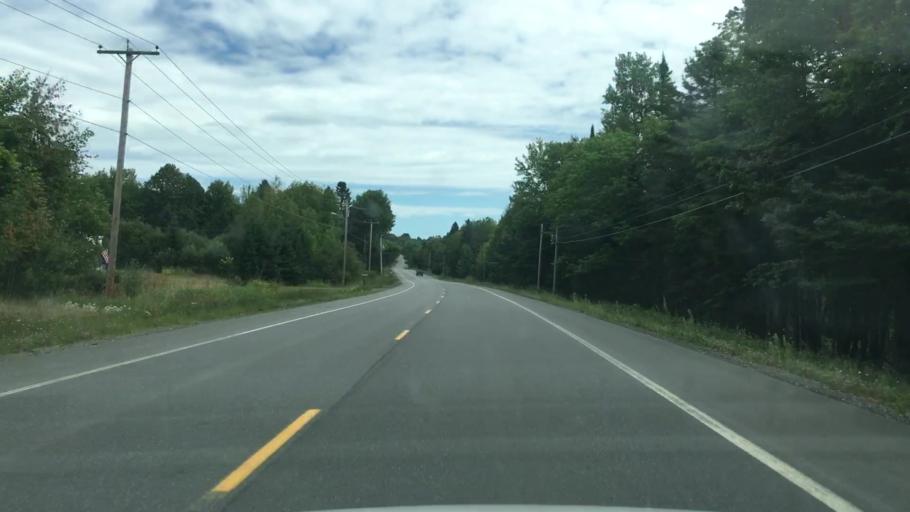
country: US
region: Maine
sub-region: Piscataquis County
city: Milo
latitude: 45.2417
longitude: -69.0323
